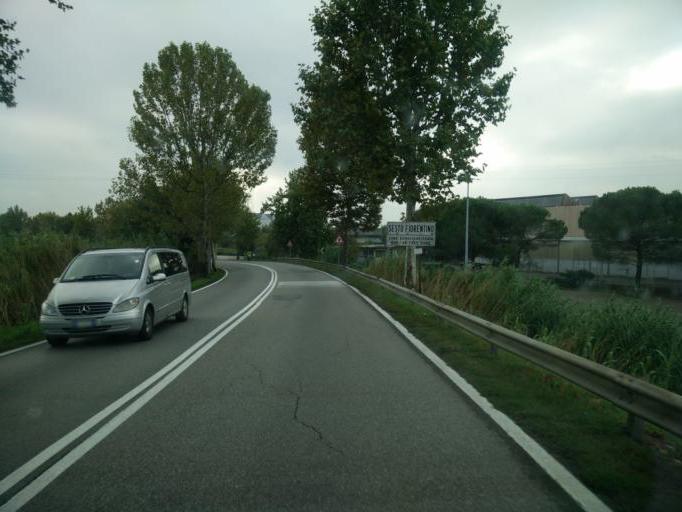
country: IT
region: Tuscany
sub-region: Province of Florence
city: San Donnino
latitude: 43.8131
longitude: 11.1562
